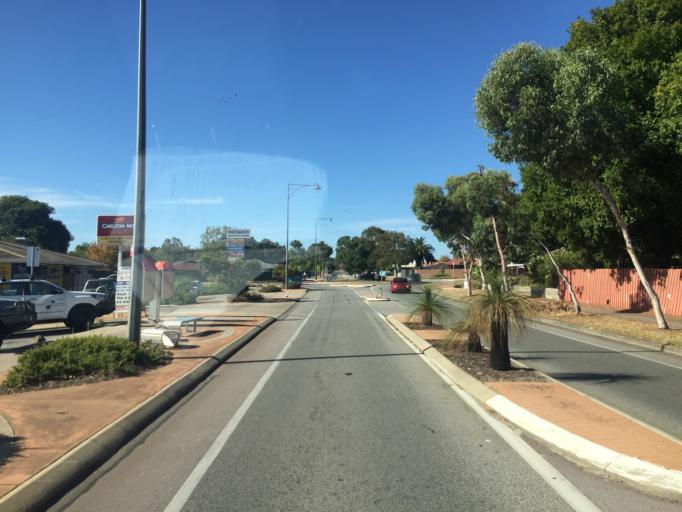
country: AU
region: Western Australia
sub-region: Gosnells
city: Kenwick
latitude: -32.0340
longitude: 115.9822
